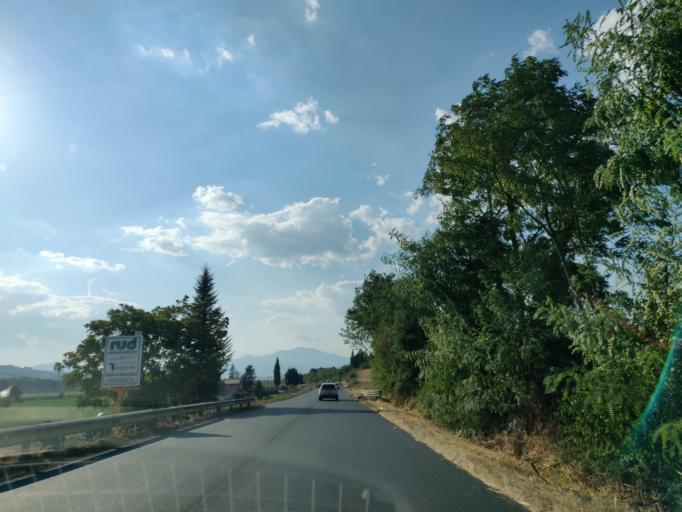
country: IT
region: Latium
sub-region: Provincia di Viterbo
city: Proceno
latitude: 42.7787
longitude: 11.8385
